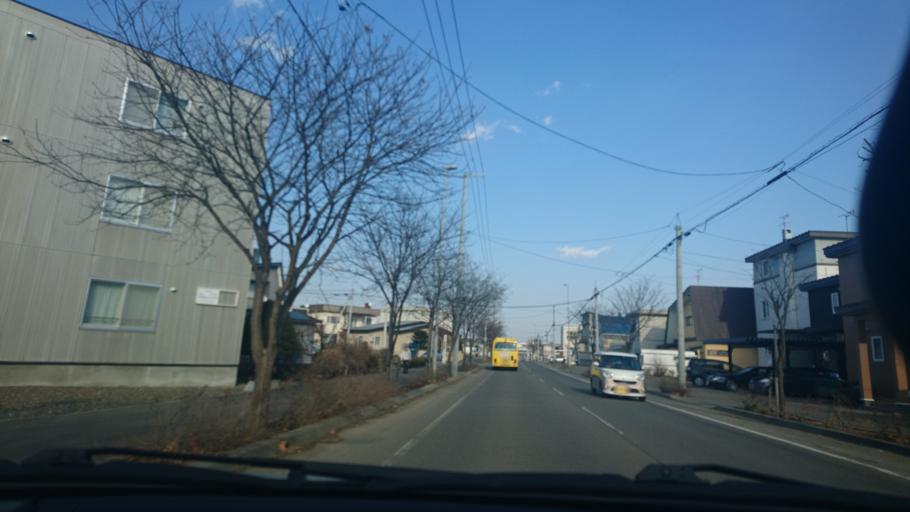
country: JP
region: Hokkaido
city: Obihiro
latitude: 42.9247
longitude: 143.1824
